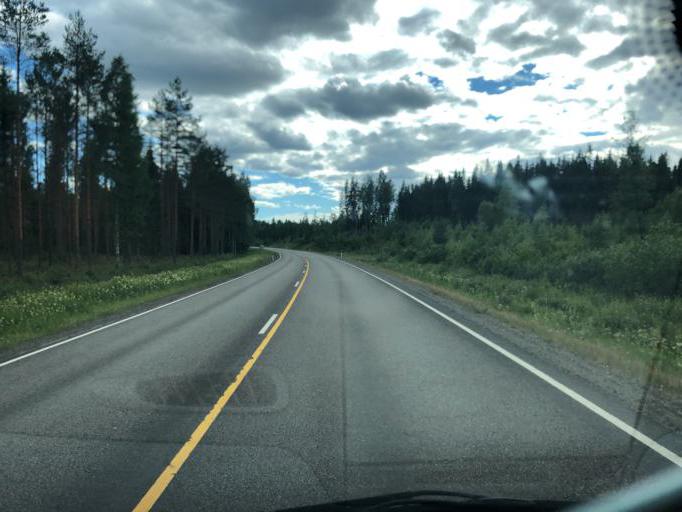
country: FI
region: Kymenlaakso
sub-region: Kouvola
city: Kouvola
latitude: 61.0192
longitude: 26.9588
